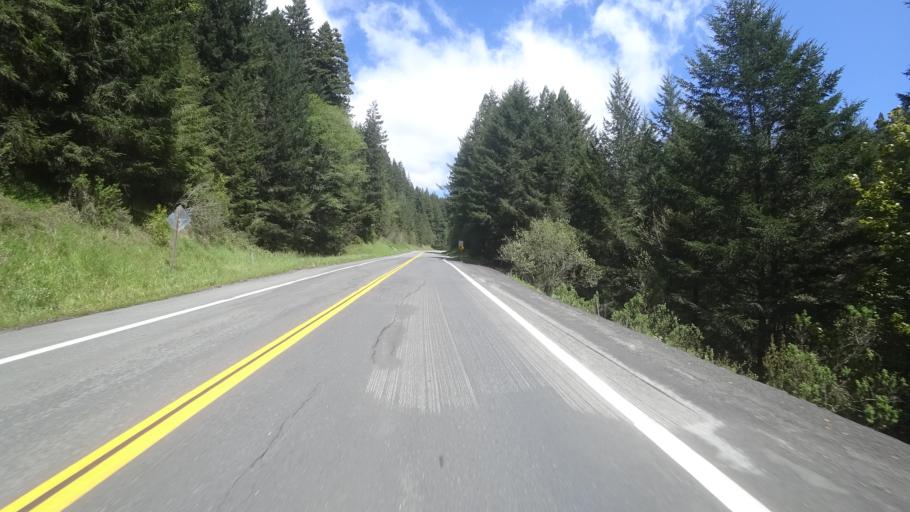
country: US
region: California
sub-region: Humboldt County
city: Blue Lake
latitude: 40.9165
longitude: -123.9143
